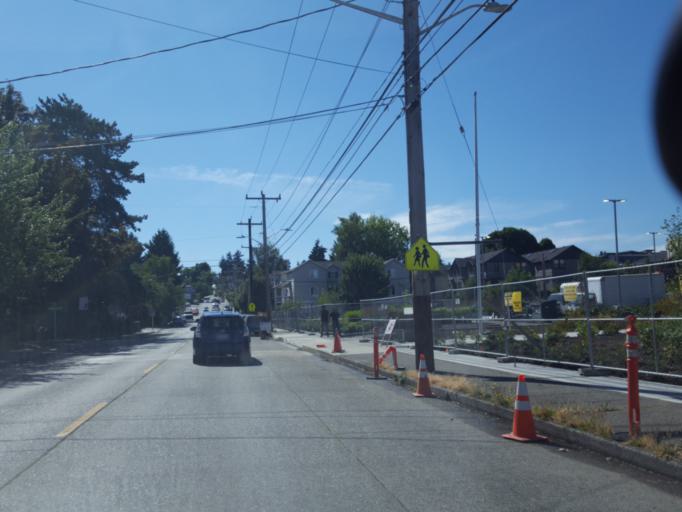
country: US
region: Washington
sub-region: King County
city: Shoreline
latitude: 47.6942
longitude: -122.3407
